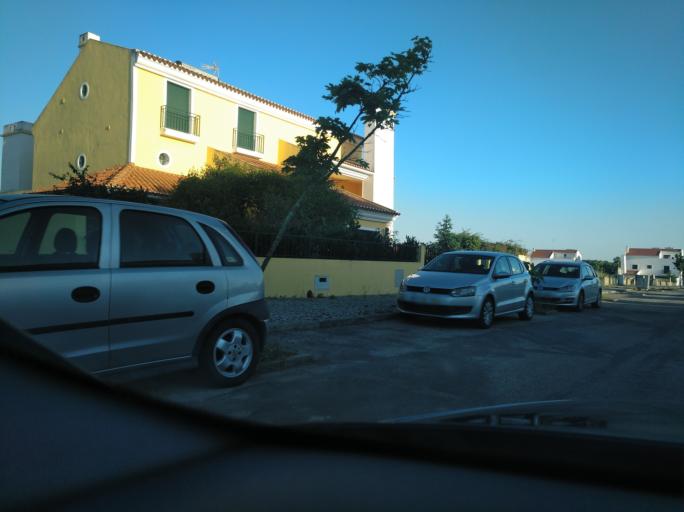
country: PT
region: Portalegre
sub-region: Elvas
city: Elvas
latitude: 38.8767
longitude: -7.1924
